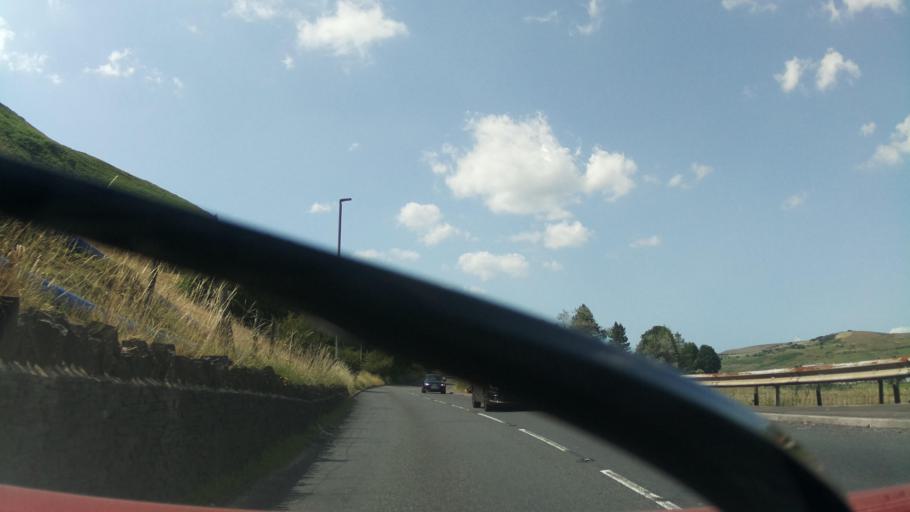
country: GB
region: Wales
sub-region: Caerphilly County Borough
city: New Tredegar
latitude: 51.7300
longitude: -3.2585
